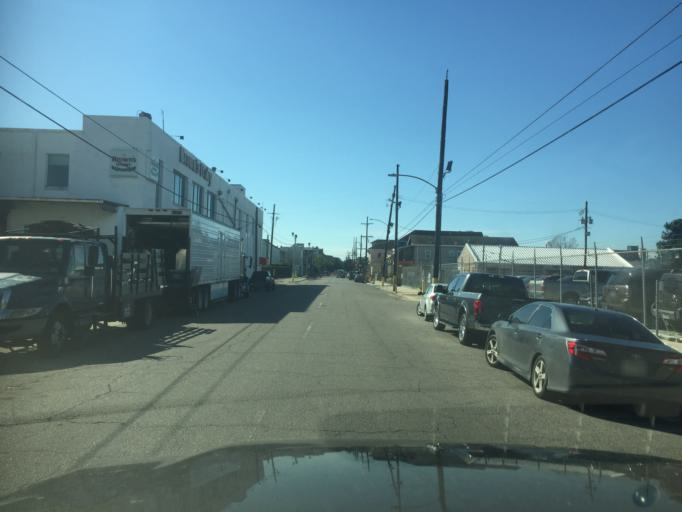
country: US
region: Louisiana
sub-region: Orleans Parish
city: New Orleans
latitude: 29.9419
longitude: -90.0769
